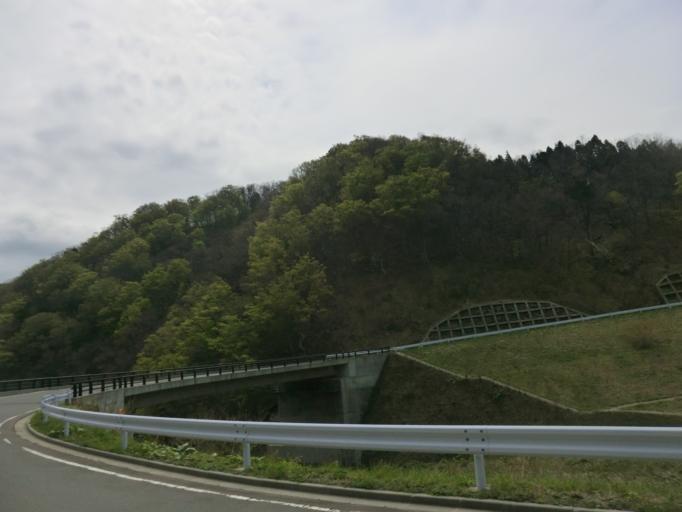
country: JP
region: Aomori
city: Mutsu
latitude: 41.3656
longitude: 140.8327
